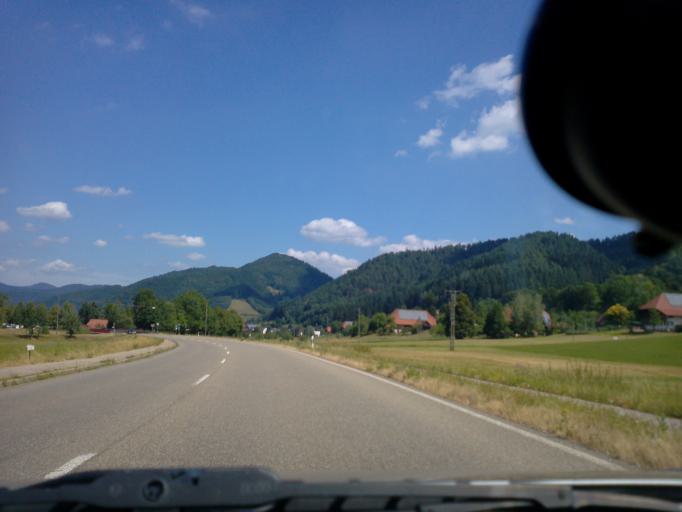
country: DE
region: Baden-Wuerttemberg
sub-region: Freiburg Region
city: Gutach (Schwarzwaldbahn)
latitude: 48.2403
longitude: 8.2144
